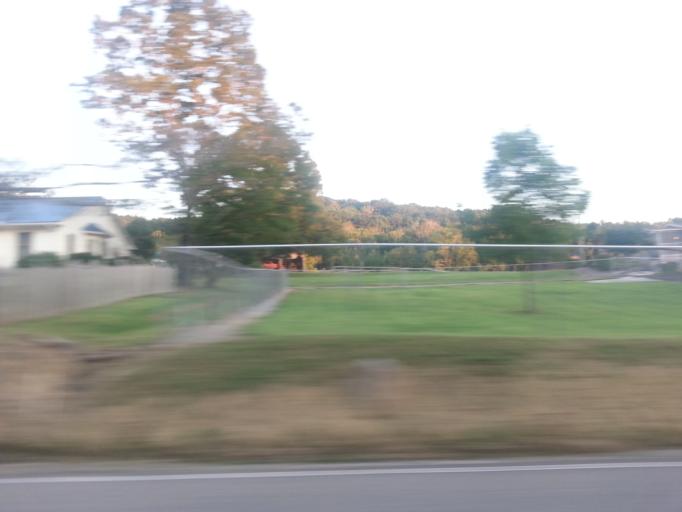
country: US
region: Tennessee
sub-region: Sevier County
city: Seymour
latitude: 35.9181
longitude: -83.7811
